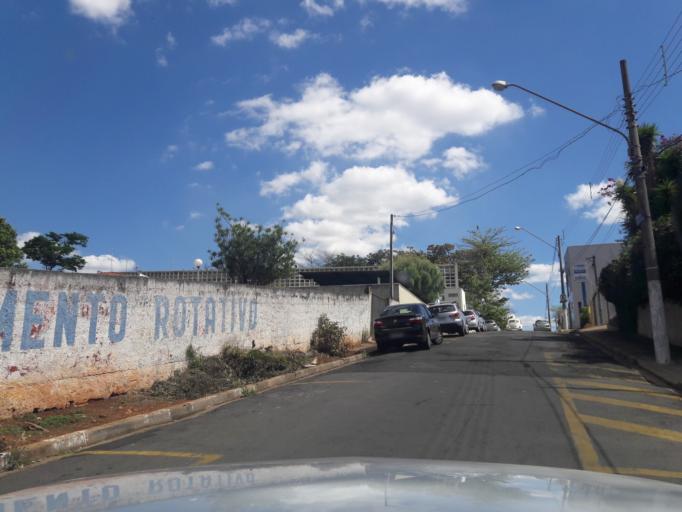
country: BR
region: Sao Paulo
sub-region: Moji-Guacu
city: Mogi-Gaucu
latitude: -22.3677
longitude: -46.9442
